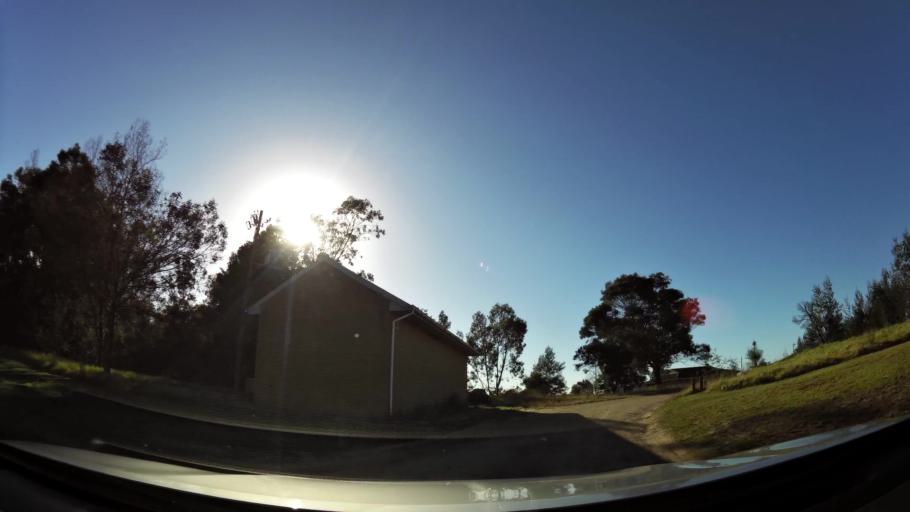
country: ZA
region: Western Cape
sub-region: Eden District Municipality
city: George
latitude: -33.9658
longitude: 22.4383
